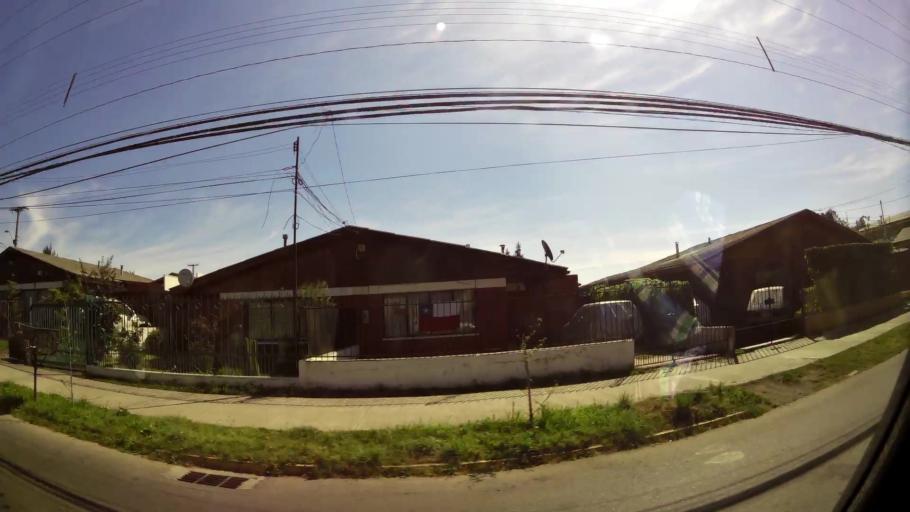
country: CL
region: Santiago Metropolitan
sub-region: Provincia de Santiago
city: Lo Prado
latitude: -33.5020
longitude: -70.7173
